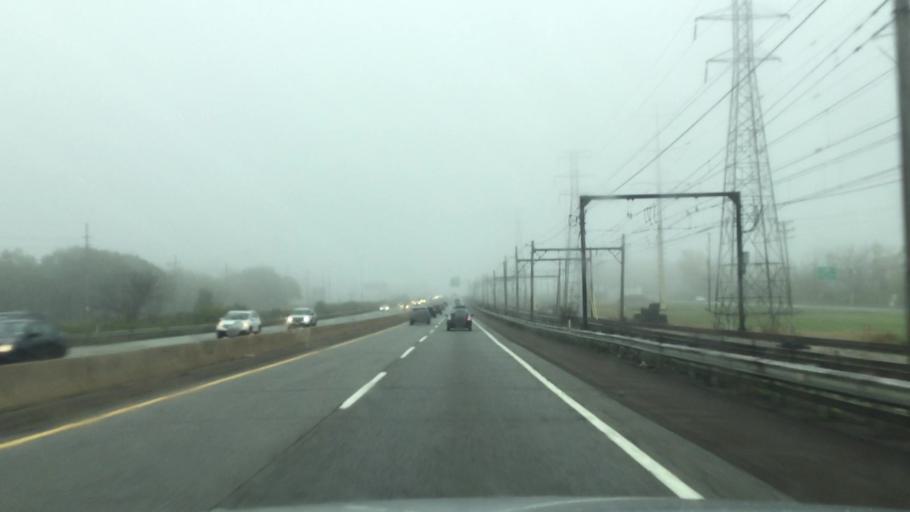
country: US
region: Indiana
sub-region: Lake County
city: East Chicago
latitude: 41.6106
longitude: -87.4570
